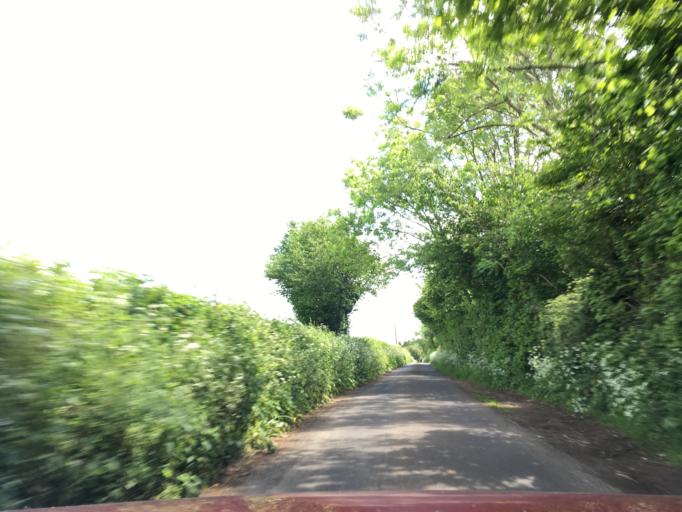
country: GB
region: England
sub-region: Gloucestershire
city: Painswick
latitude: 51.7863
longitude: -2.1432
